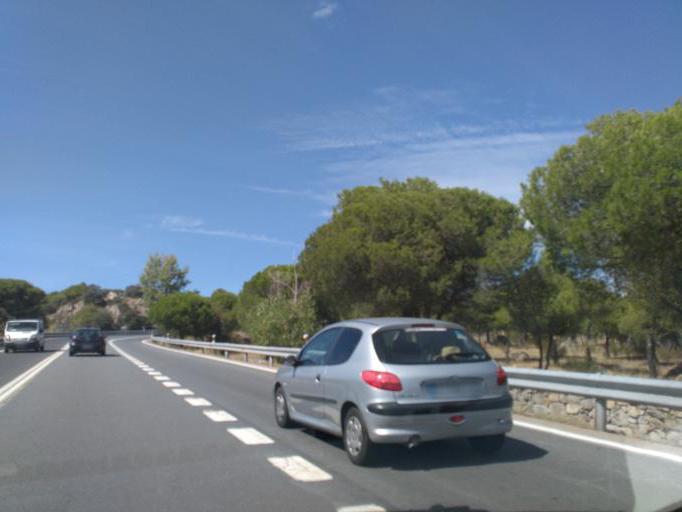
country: ES
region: Madrid
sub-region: Provincia de Madrid
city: Torrelodones
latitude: 40.5531
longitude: -3.9597
